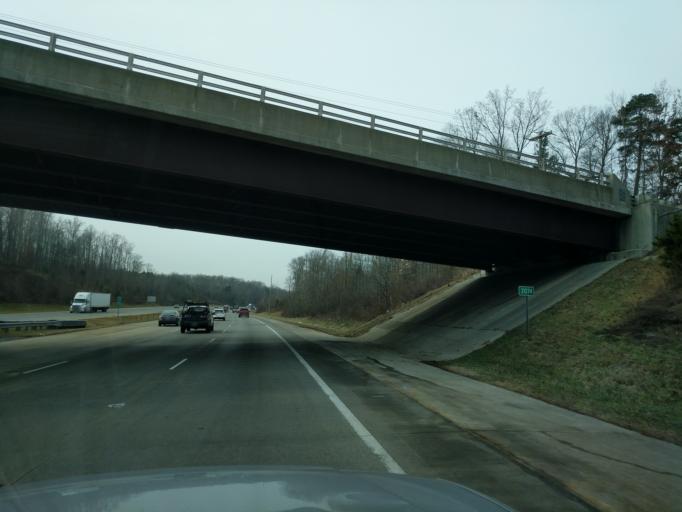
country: US
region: North Carolina
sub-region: Mecklenburg County
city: Huntersville
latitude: 35.3439
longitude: -80.8813
